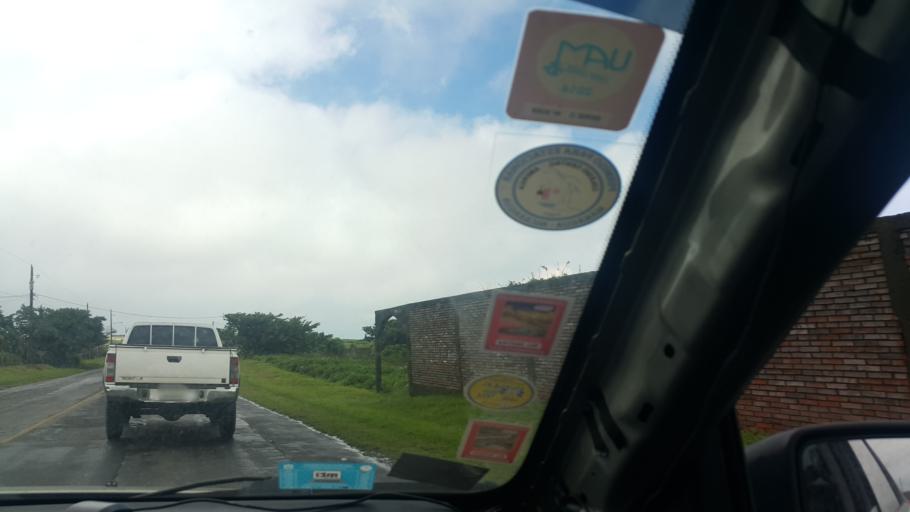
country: NI
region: Managua
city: El Crucero
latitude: 11.9500
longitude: -86.3008
